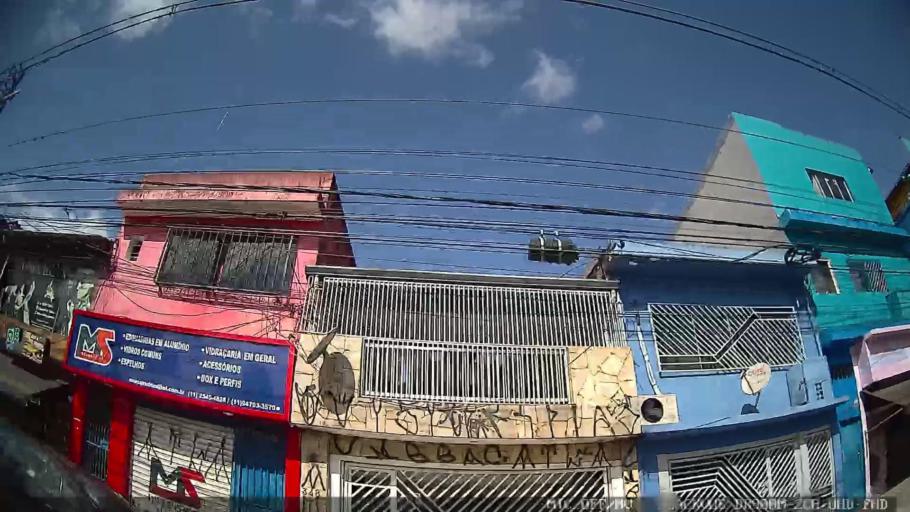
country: BR
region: Sao Paulo
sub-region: Guarulhos
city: Guarulhos
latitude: -23.4963
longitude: -46.4681
